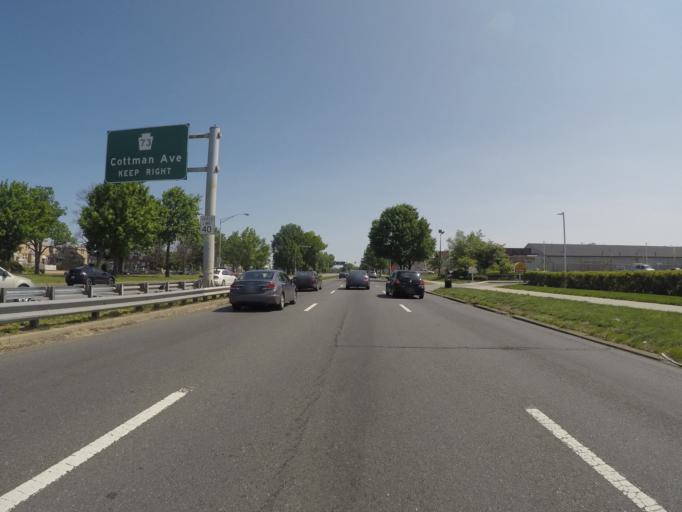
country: US
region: New Jersey
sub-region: Burlington County
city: Palmyra
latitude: 40.0404
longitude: -75.0583
